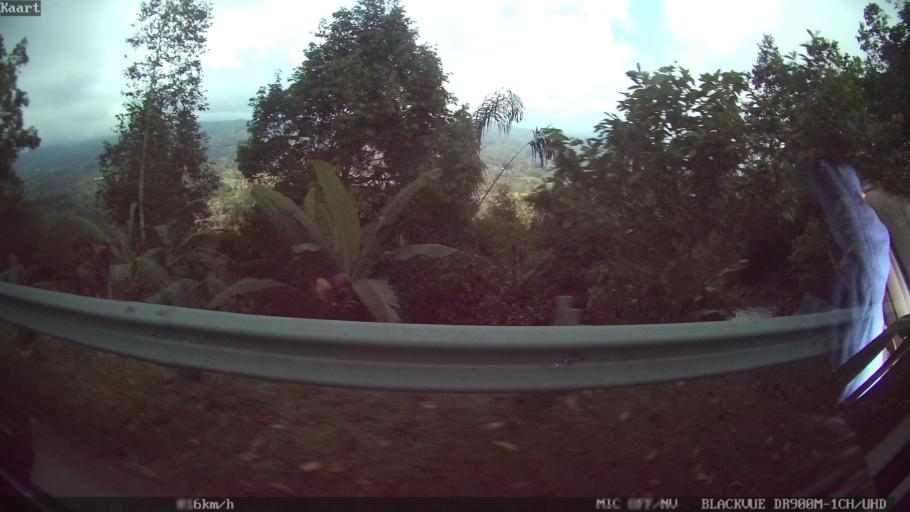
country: ID
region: Bali
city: Peneng
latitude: -8.3654
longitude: 115.2119
